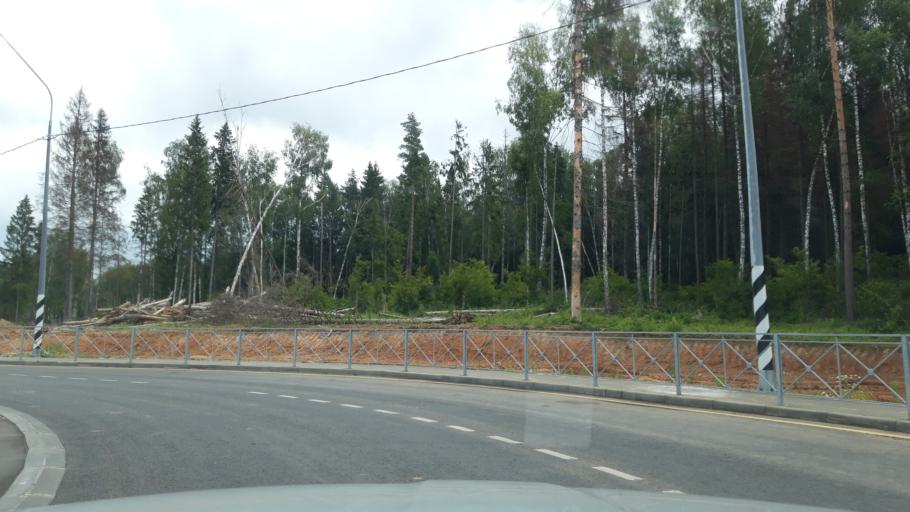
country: RU
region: Moskovskaya
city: Lozhki
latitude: 56.0803
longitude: 37.1150
